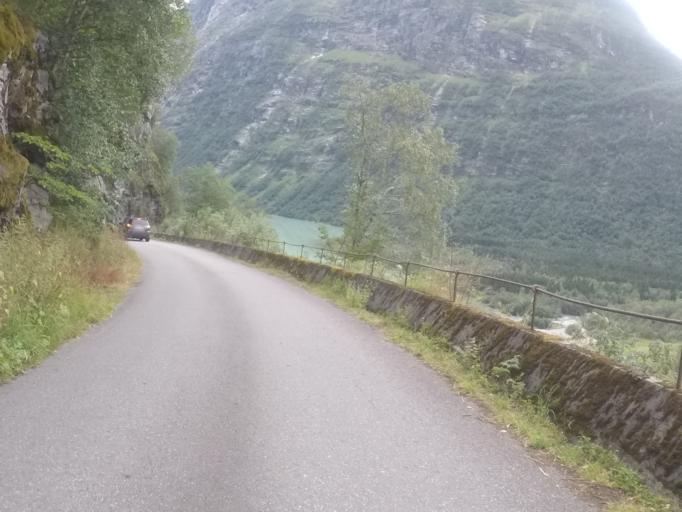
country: NO
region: Sogn og Fjordane
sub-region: Stryn
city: Stryn
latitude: 61.7897
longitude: 6.9979
